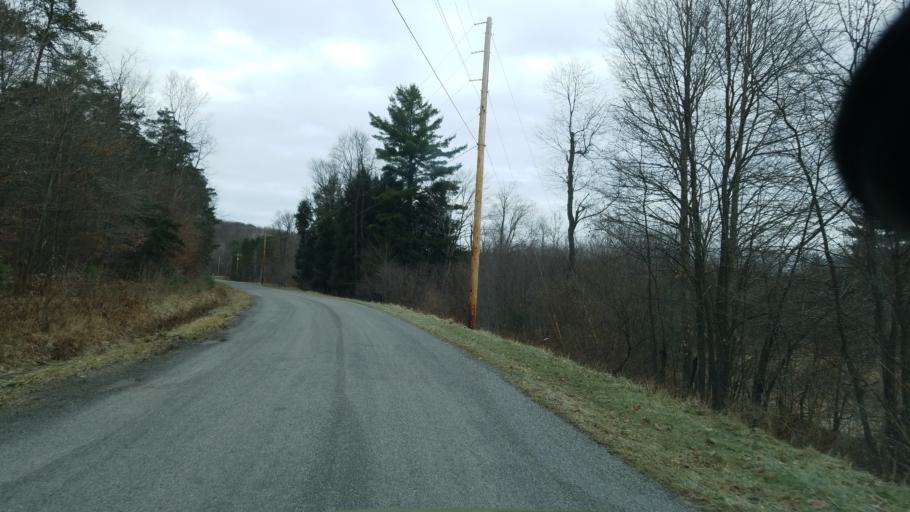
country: US
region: Pennsylvania
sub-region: Clearfield County
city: Treasure Lake
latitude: 41.1322
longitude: -78.6031
